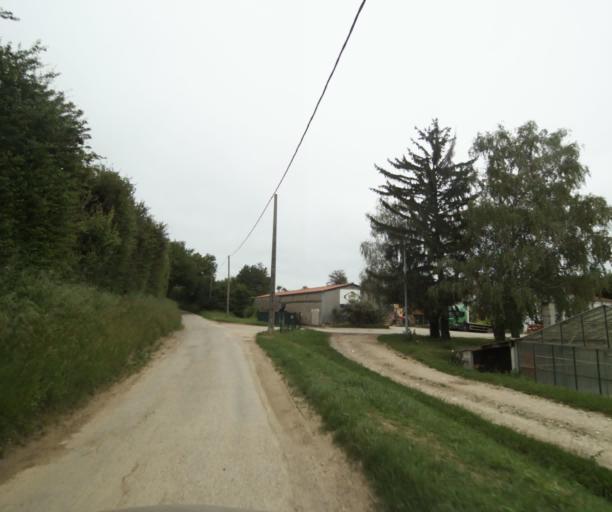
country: FR
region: Rhone-Alpes
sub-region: Departement du Rhone
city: Rillieux-la-Pape
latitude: 45.8510
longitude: 4.9144
